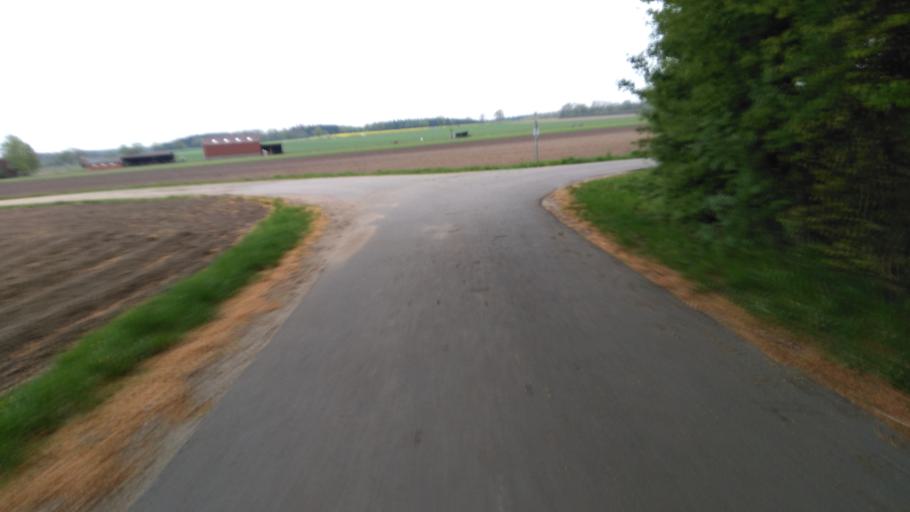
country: DE
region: Lower Saxony
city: Harsefeld
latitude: 53.4543
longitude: 9.5347
